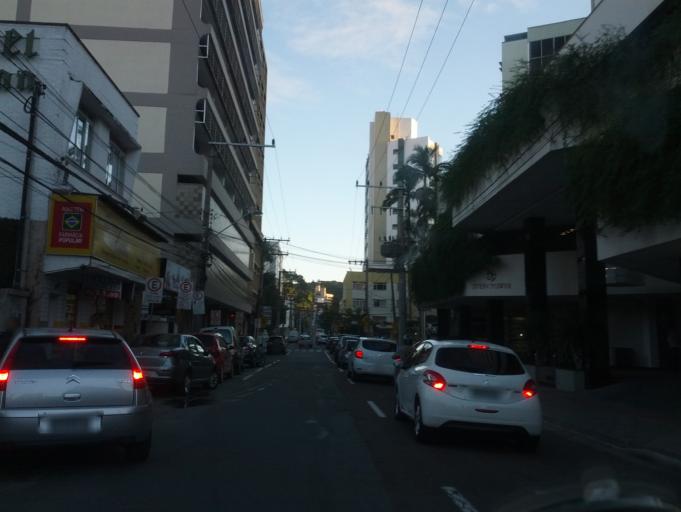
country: BR
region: Santa Catarina
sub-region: Blumenau
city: Blumenau
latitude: -26.9232
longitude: -49.0641
